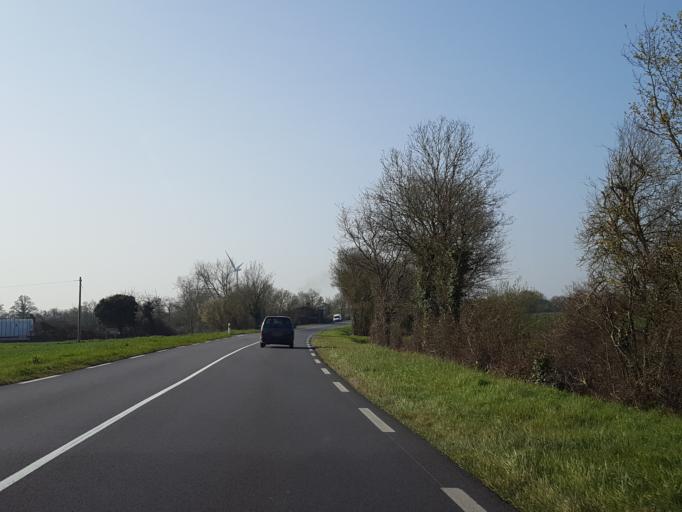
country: FR
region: Pays de la Loire
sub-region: Departement de la Vendee
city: Saint-Philbert-de-Bouaine
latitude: 47.0158
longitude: -1.5038
